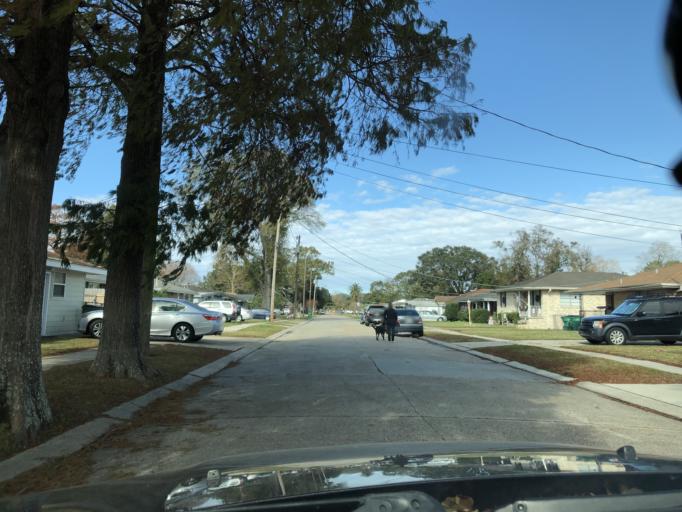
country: US
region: Louisiana
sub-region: Jefferson Parish
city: Metairie Terrace
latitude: 29.9823
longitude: -90.1694
